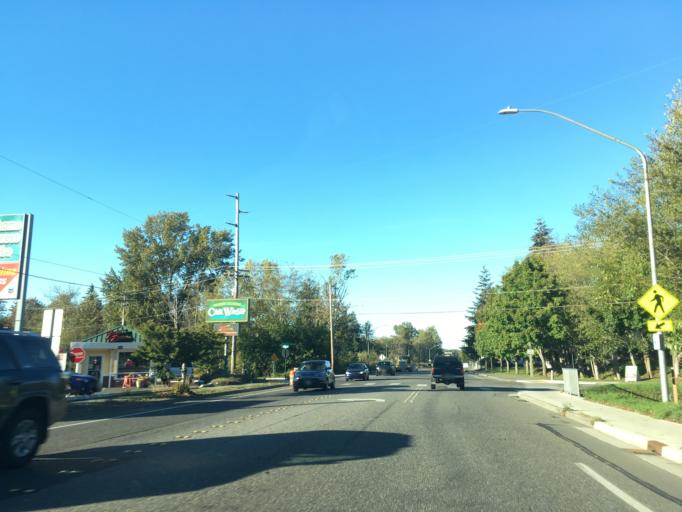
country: US
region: Washington
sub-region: Whatcom County
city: Bellingham
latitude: 48.7362
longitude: -122.4656
